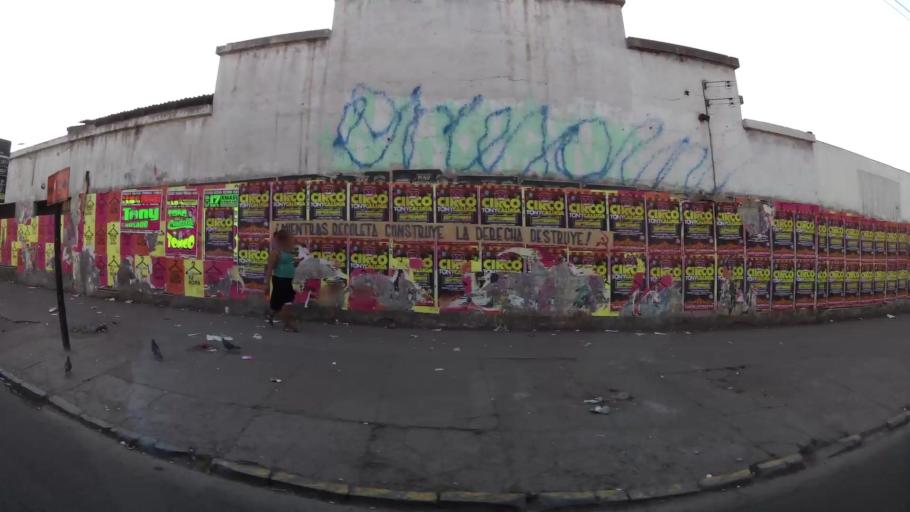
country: CL
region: Santiago Metropolitan
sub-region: Provincia de Santiago
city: Santiago
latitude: -33.3985
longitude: -70.6281
